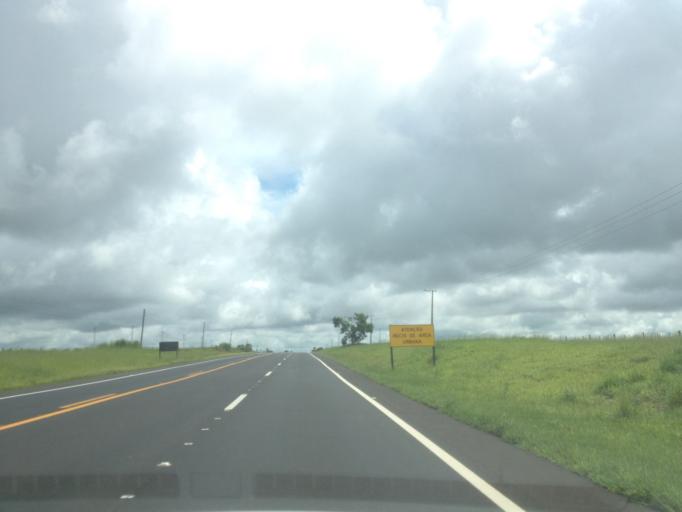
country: BR
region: Sao Paulo
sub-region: Marilia
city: Marilia
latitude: -22.2615
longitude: -49.9940
